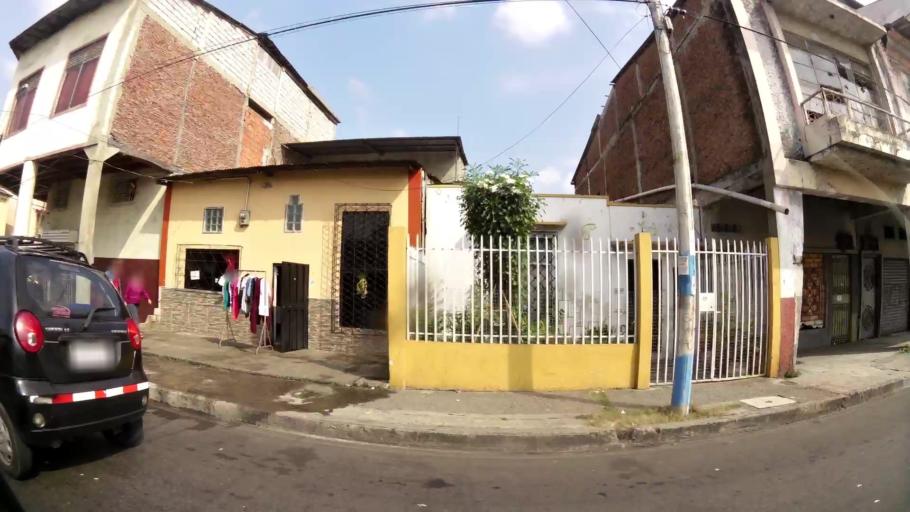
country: EC
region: Guayas
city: Guayaquil
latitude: -2.2018
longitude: -79.9009
